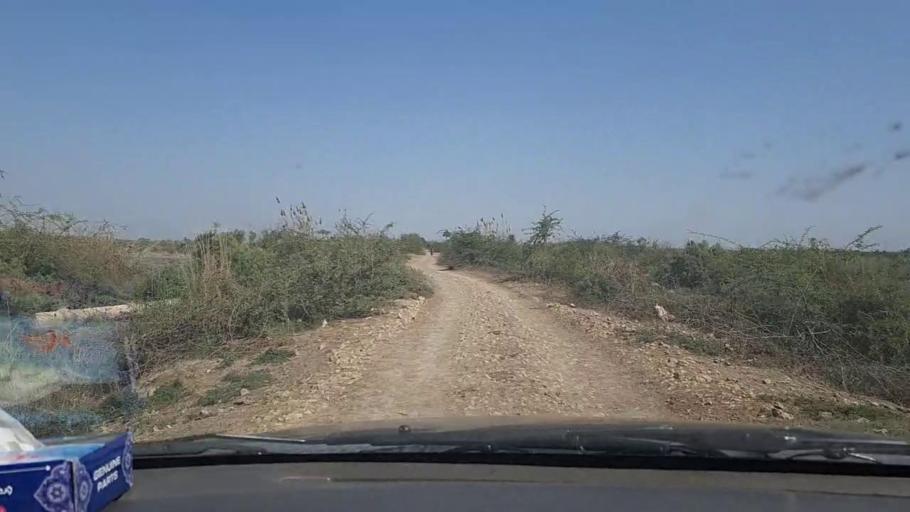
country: PK
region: Sindh
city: Chuhar Jamali
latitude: 24.2742
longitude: 67.7370
